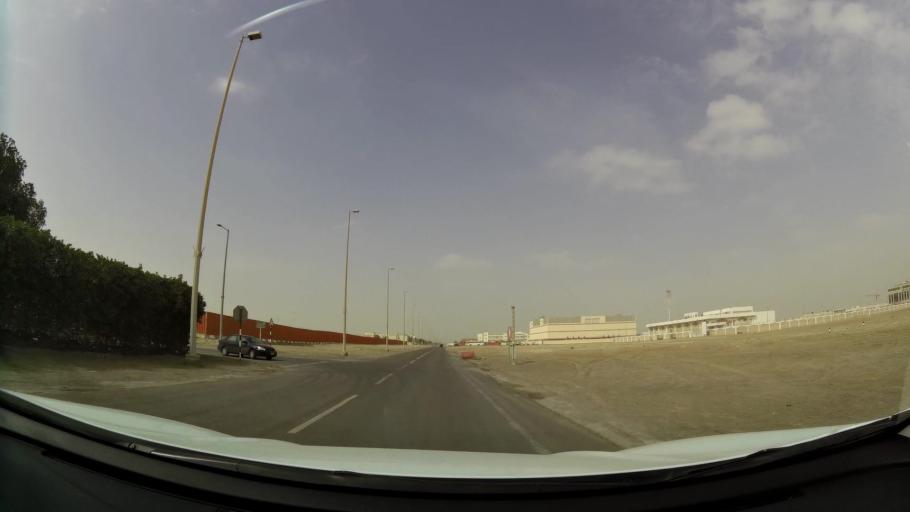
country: AE
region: Abu Dhabi
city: Abu Dhabi
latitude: 24.4094
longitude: 54.5674
